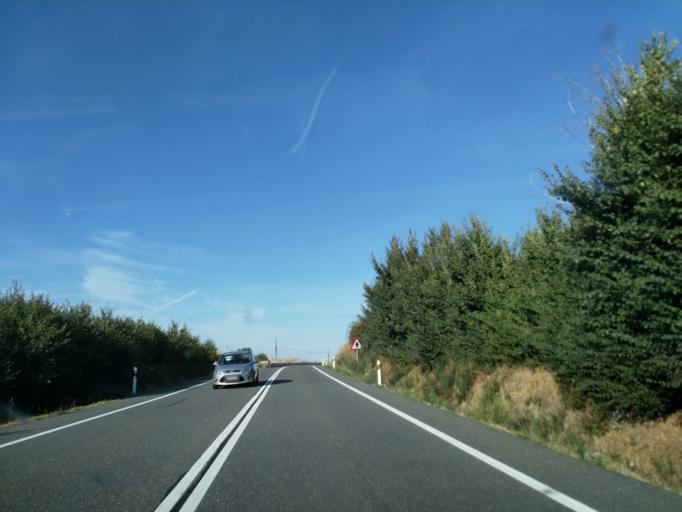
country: ES
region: Castille and Leon
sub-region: Provincia de Segovia
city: Villacastin
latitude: 40.7853
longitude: -4.4055
